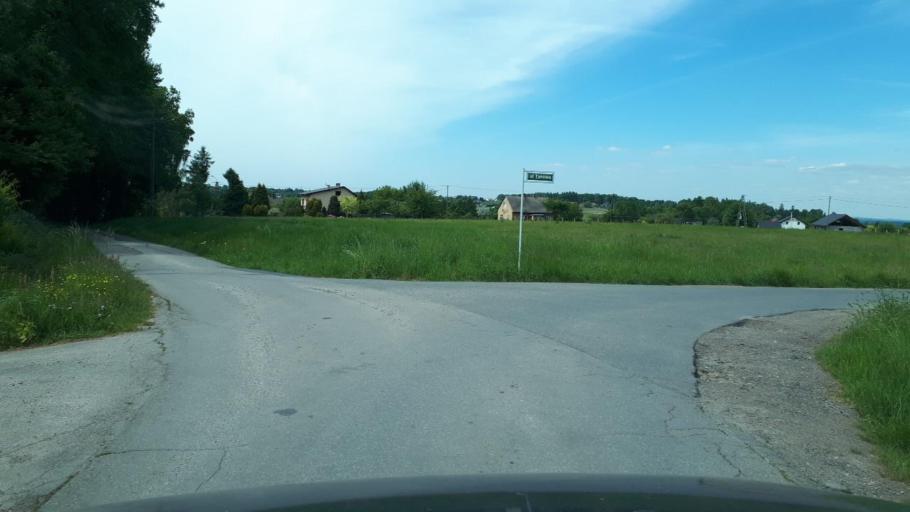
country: PL
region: Silesian Voivodeship
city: Janowice
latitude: 49.8871
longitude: 19.1023
